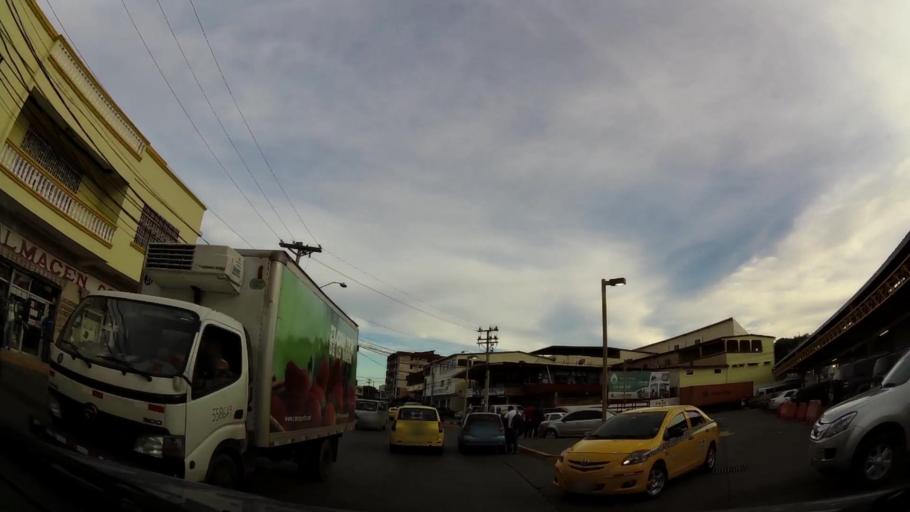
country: PA
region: Panama
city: La Chorrera
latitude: 8.8785
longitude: -79.7815
